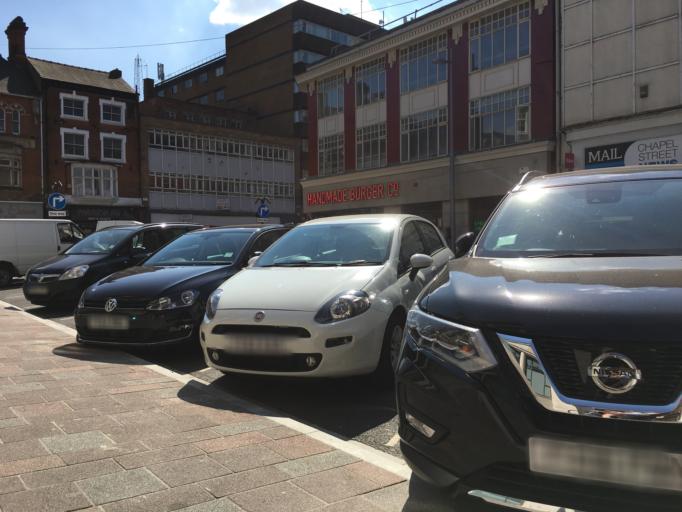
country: GB
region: England
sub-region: City of Kingston upon Hull
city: Hull
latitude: 53.7444
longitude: -0.3419
